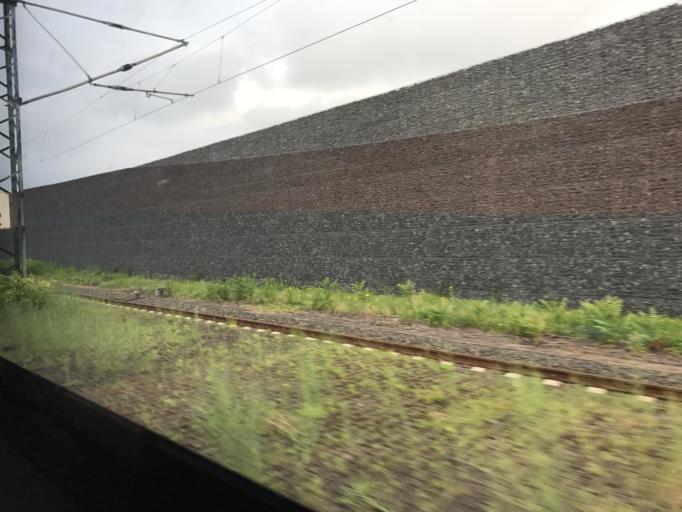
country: DE
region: Rheinland-Pfalz
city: Bingen am Rhein
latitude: 49.9698
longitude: 7.9062
